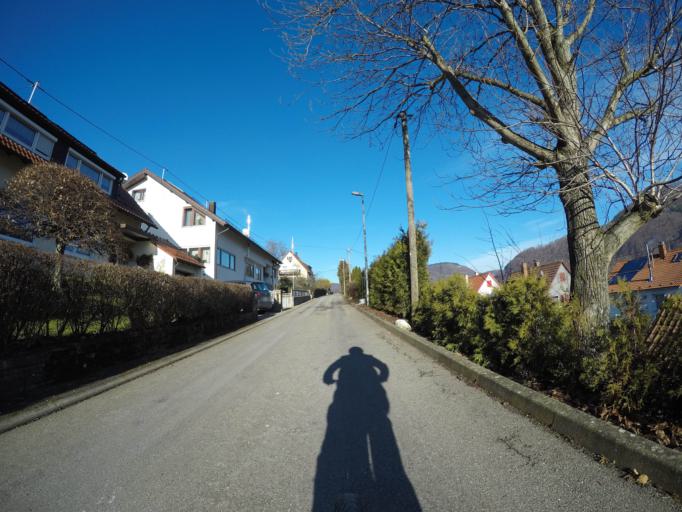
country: DE
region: Baden-Wuerttemberg
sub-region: Tuebingen Region
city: Pfullingen
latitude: 48.4324
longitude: 9.2539
